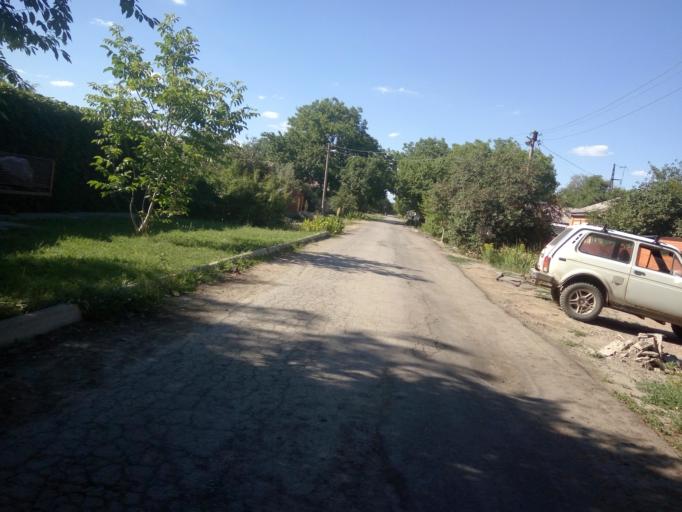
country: RU
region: Rostov
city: Bataysk
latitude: 47.1403
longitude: 39.7710
